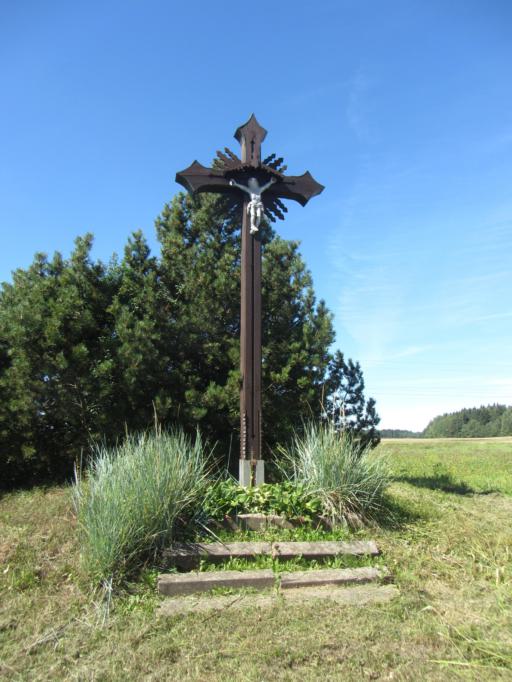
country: LT
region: Panevezys
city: Rokiskis
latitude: 55.9137
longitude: 25.6280
